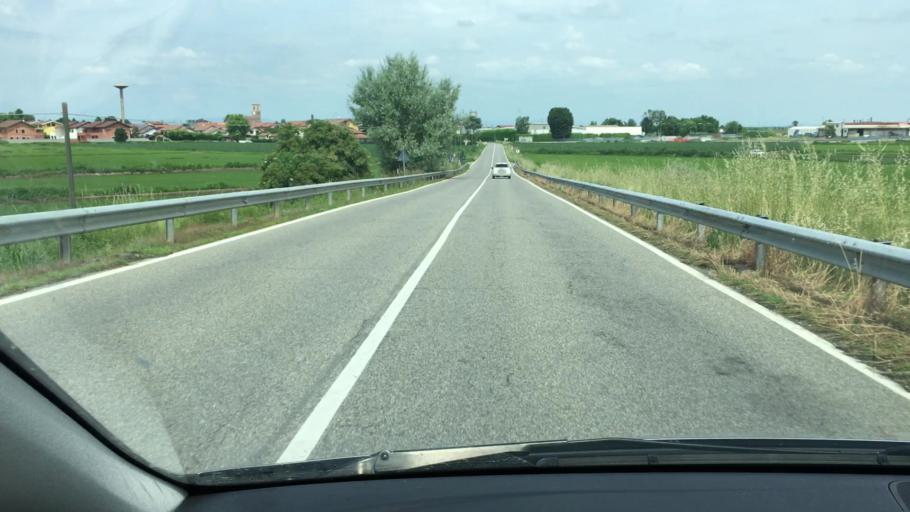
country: IT
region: Piedmont
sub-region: Provincia di Novara
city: Casalbeltrame
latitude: 45.4300
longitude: 8.4645
